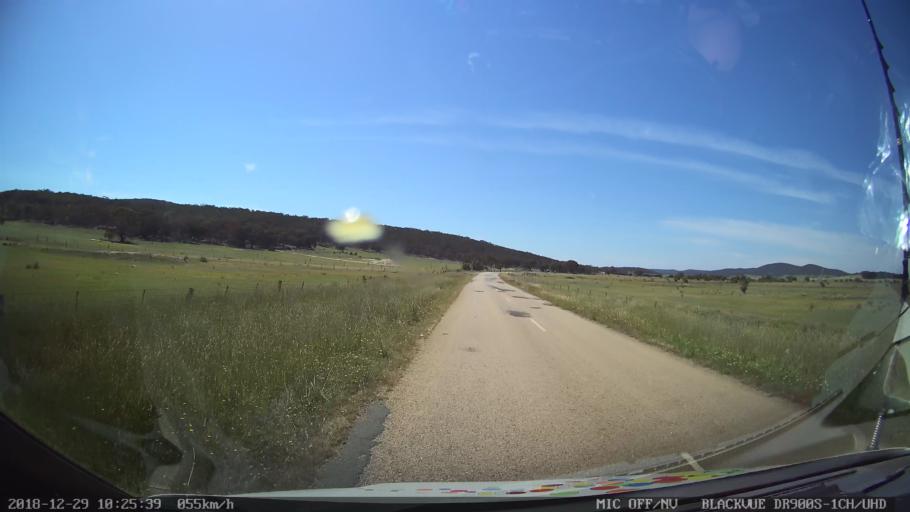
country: AU
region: New South Wales
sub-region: Yass Valley
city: Gundaroo
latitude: -34.9193
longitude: 149.4388
